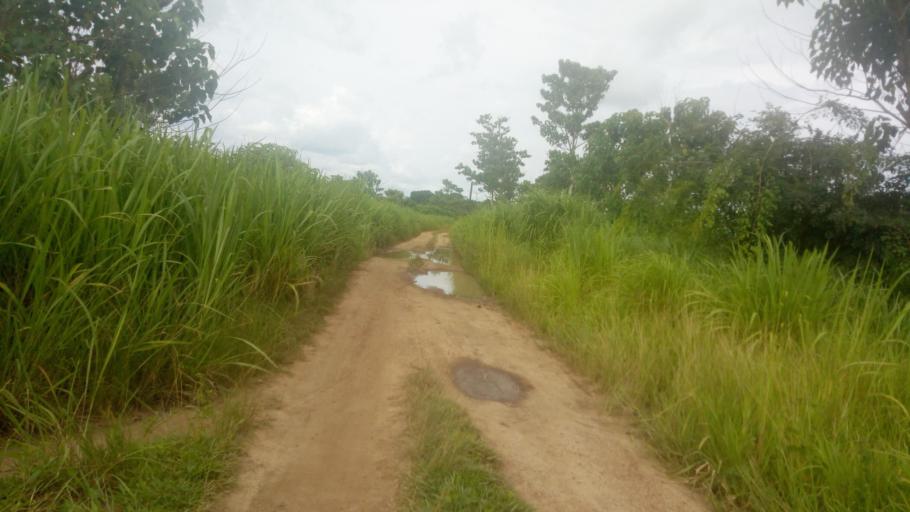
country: SL
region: Northern Province
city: Magburaka
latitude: 8.6731
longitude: -12.0231
